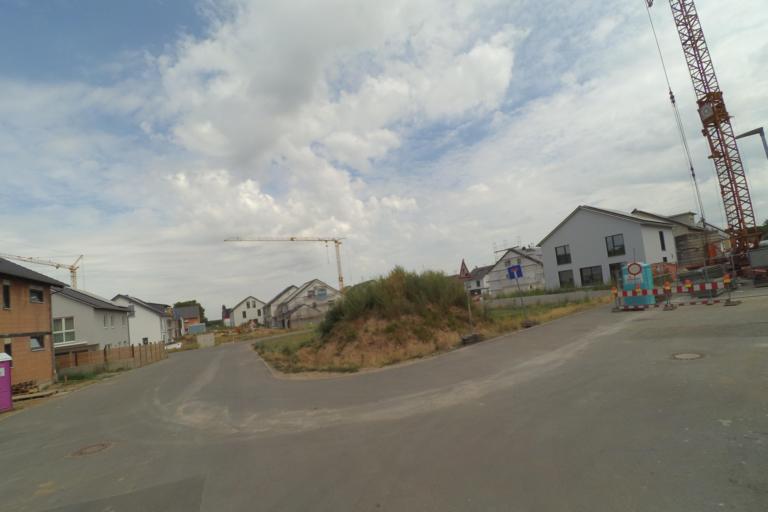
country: DE
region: Hesse
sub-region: Regierungsbezirk Darmstadt
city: Einhausen
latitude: 49.7076
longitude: 8.5708
